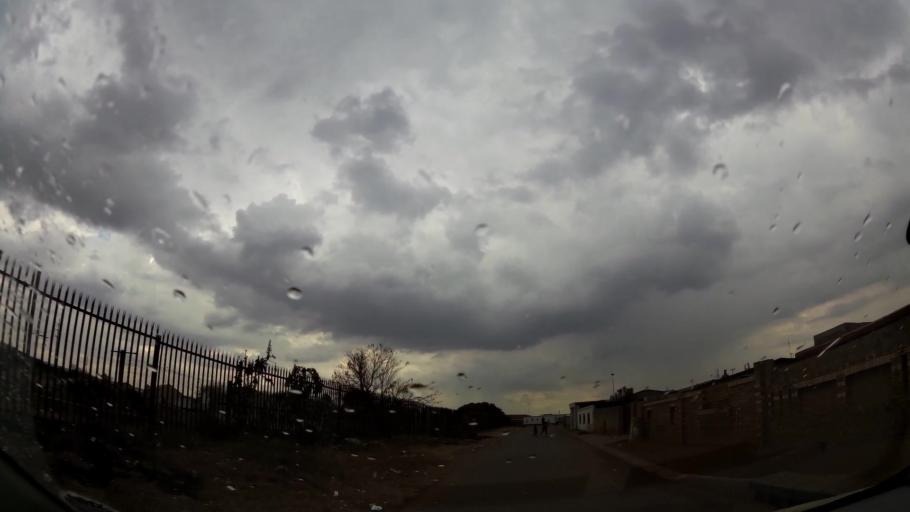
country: ZA
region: Gauteng
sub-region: Ekurhuleni Metropolitan Municipality
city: Germiston
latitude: -26.3592
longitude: 28.1601
